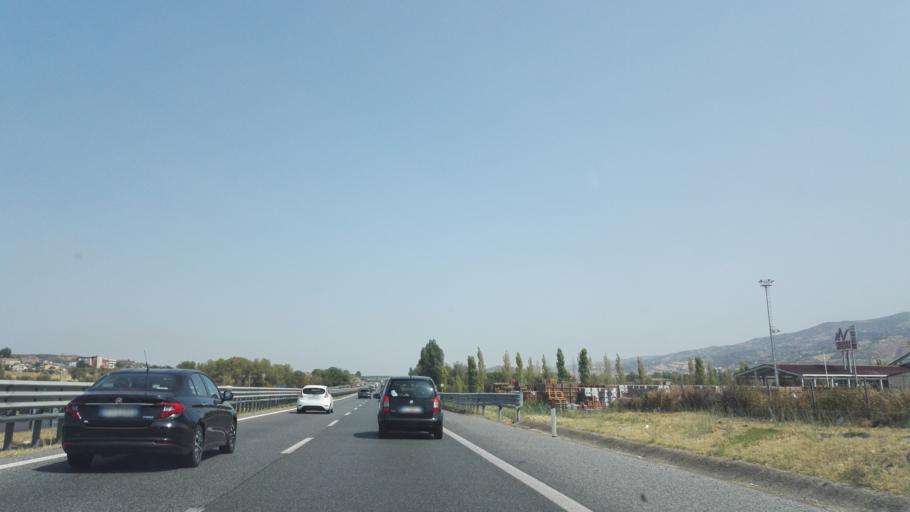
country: IT
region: Calabria
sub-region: Provincia di Cosenza
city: Settimo
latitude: 39.3960
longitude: 16.2430
